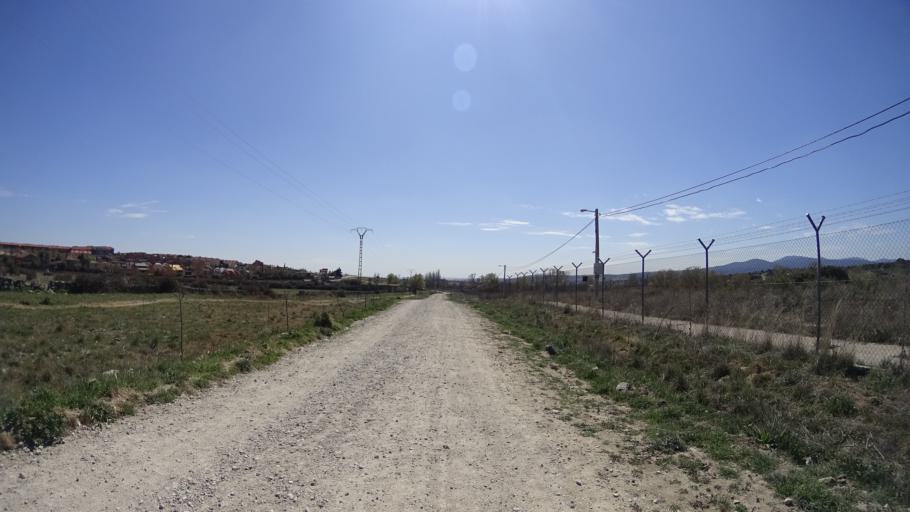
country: ES
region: Madrid
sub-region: Provincia de Madrid
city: Colmenar Viejo
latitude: 40.6752
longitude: -3.7846
